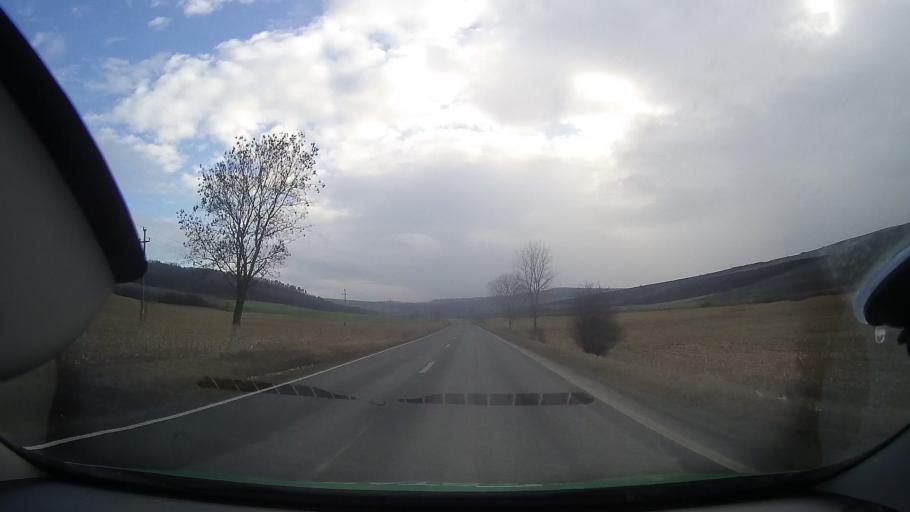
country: RO
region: Mures
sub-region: Comuna Cucerdea
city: Cucerdea
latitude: 46.3753
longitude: 24.2577
